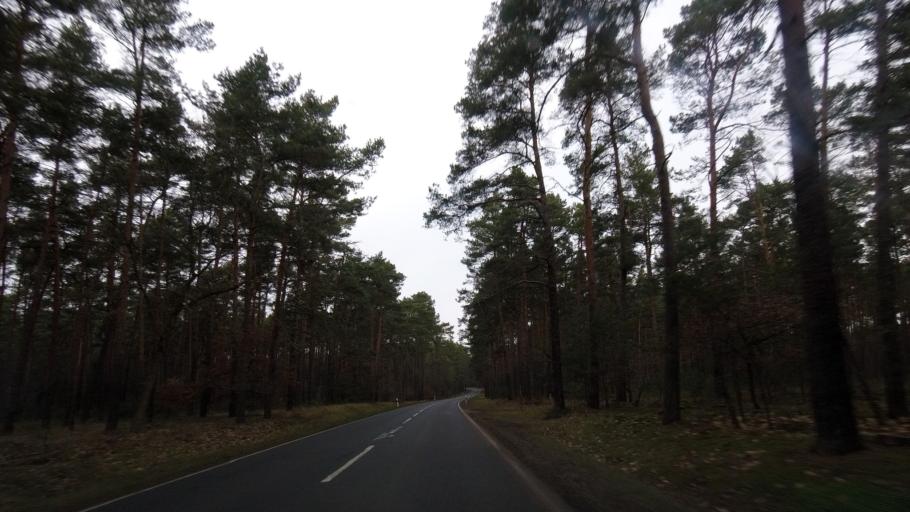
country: DE
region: Brandenburg
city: Niedergorsdorf
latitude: 52.0272
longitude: 12.9489
